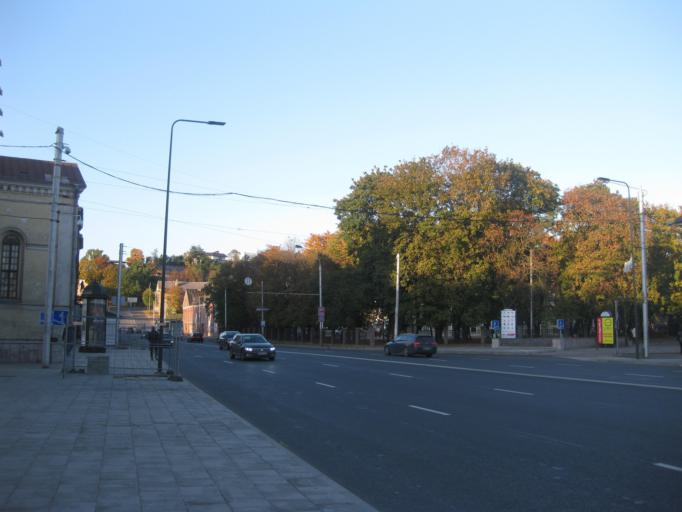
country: LT
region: Kauno apskritis
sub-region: Kaunas
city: Kaunas
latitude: 54.8964
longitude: 23.8958
